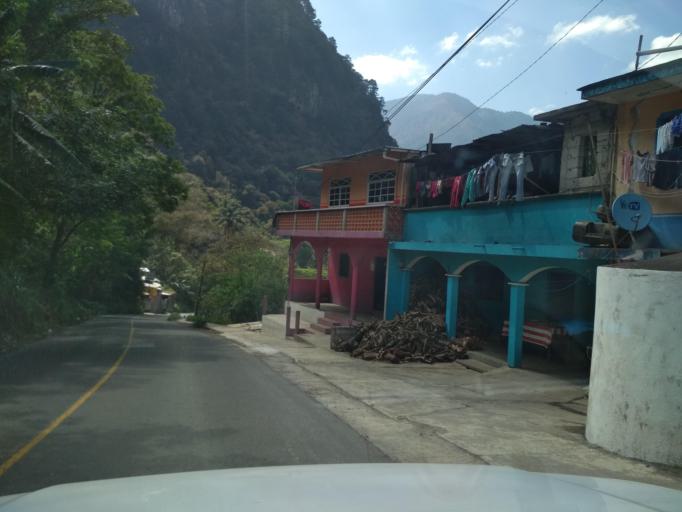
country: MX
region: Veracruz
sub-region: Tlilapan
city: Tonalixco
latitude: 18.7849
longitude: -97.0883
